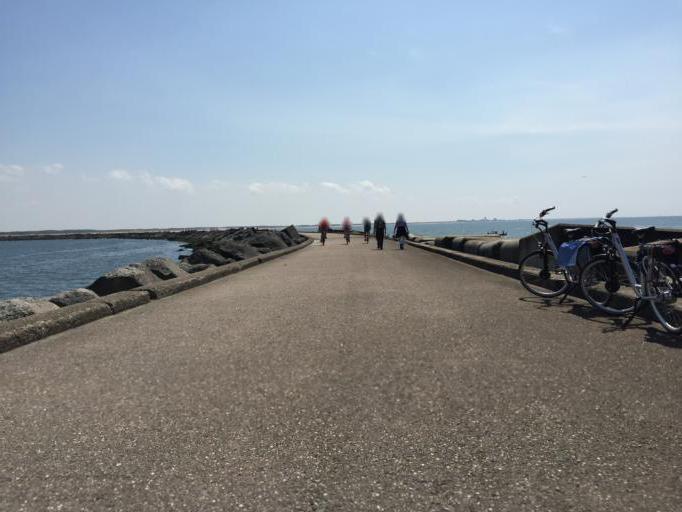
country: NL
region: North Holland
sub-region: Gemeente Zandvoort
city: Zandvoort
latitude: 52.4631
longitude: 4.5323
